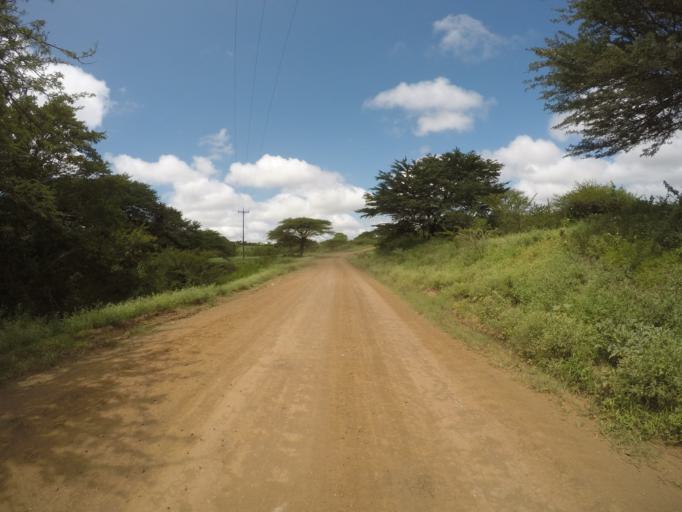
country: ZA
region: KwaZulu-Natal
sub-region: uThungulu District Municipality
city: Empangeni
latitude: -28.5714
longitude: 31.8371
